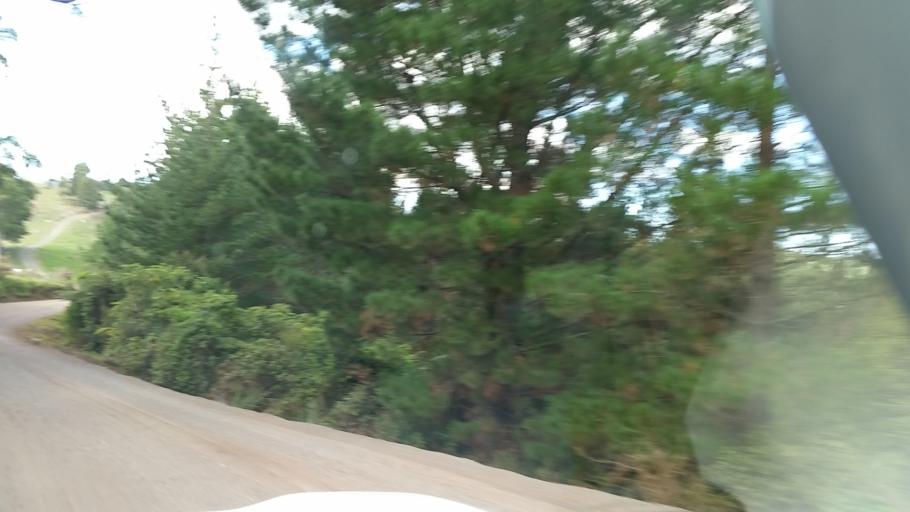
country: NZ
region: Northland
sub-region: Whangarei
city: Whangarei
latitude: -35.5962
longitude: 174.3201
